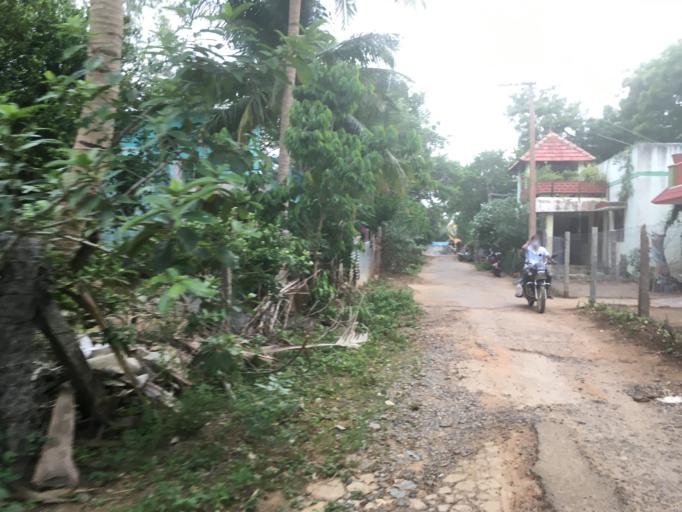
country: IN
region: Tamil Nadu
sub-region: Villupuram
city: Auroville
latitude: 12.0108
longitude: 79.8019
